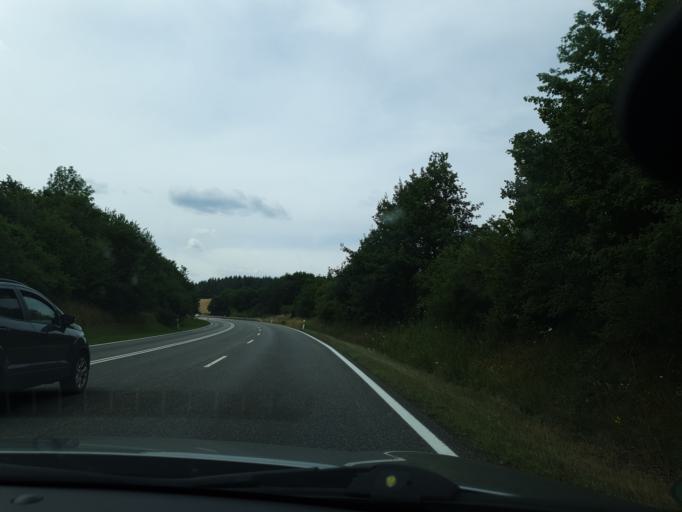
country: DE
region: Rheinland-Pfalz
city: Mayen
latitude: 50.3119
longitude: 7.2018
